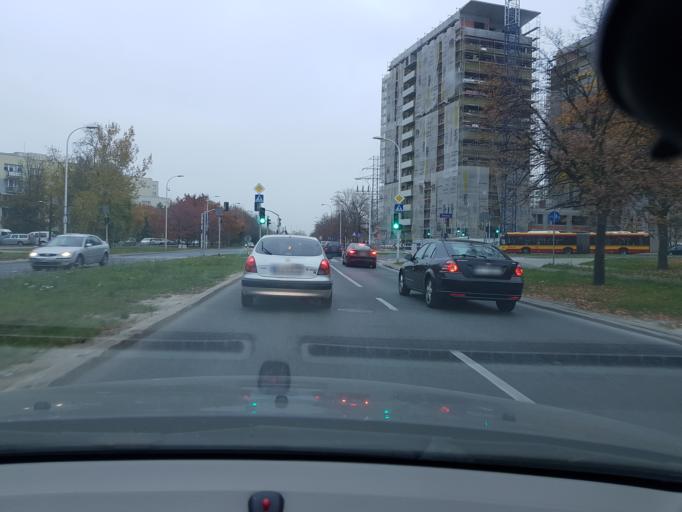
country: PL
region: Masovian Voivodeship
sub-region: Warszawa
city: Ursynow
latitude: 52.1506
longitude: 21.0345
